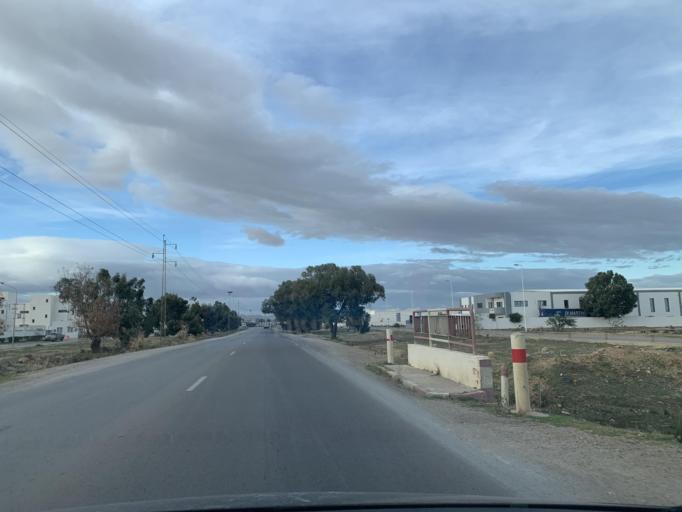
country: TN
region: Susah
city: Harqalah
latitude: 36.1077
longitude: 10.3869
